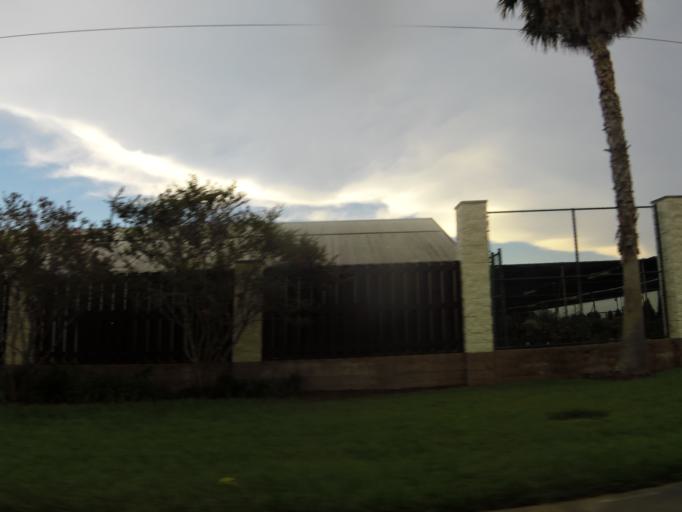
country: US
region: Florida
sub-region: Saint Johns County
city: Ponte Vedra Beach
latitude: 30.2537
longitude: -81.3943
